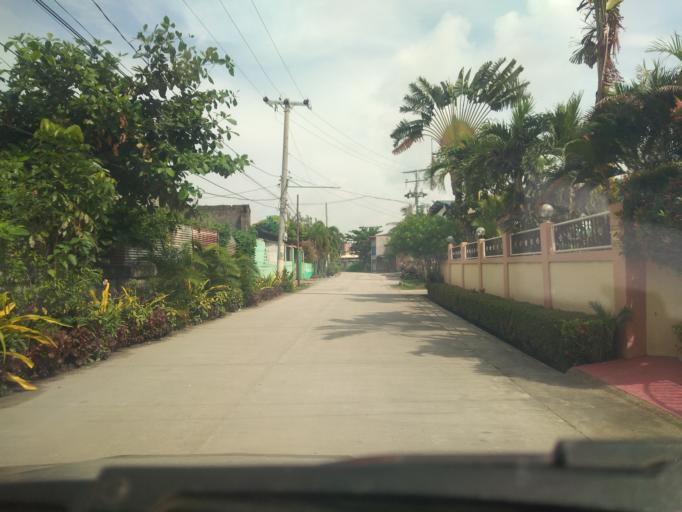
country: PH
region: Central Luzon
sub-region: Province of Pampanga
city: Pau
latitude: 15.0099
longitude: 120.7098
